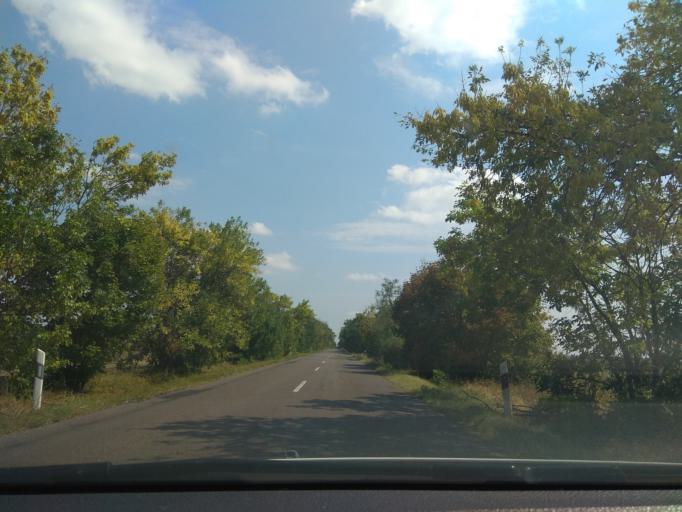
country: HU
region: Heves
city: Ostoros
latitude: 47.8268
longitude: 20.4681
